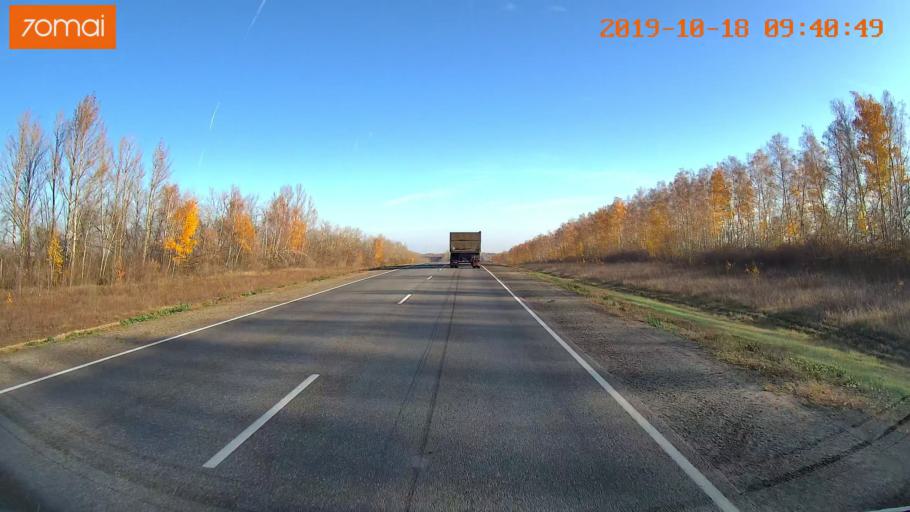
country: RU
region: Tula
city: Kazachka
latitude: 53.2684
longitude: 38.1534
